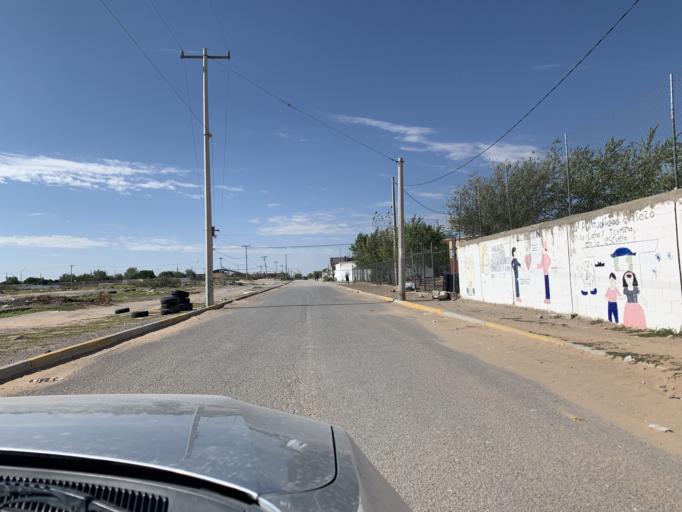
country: US
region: Texas
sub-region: El Paso County
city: San Elizario
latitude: 31.5770
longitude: -106.3440
